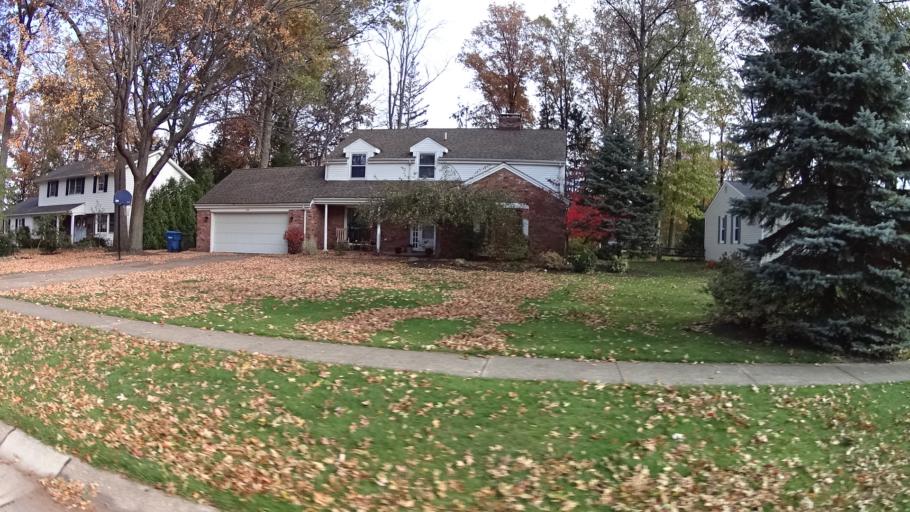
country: US
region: Ohio
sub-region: Lorain County
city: Avon Lake
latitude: 41.5087
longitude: -82.0223
